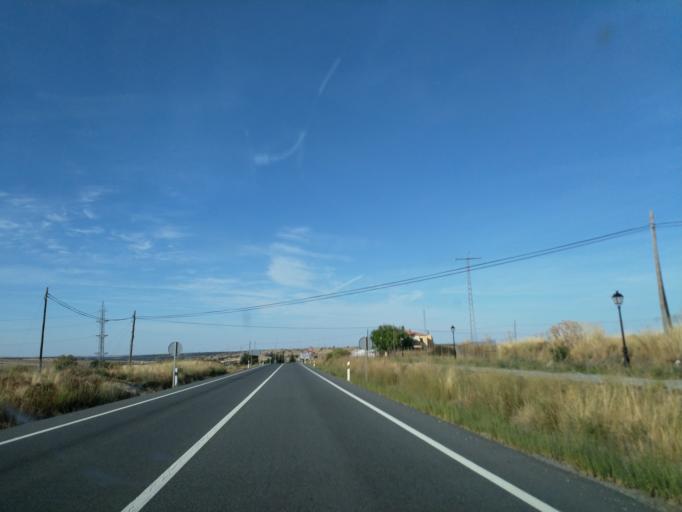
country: ES
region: Castille and Leon
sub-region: Provincia de Segovia
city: Villacastin
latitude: 40.7794
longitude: -4.4224
